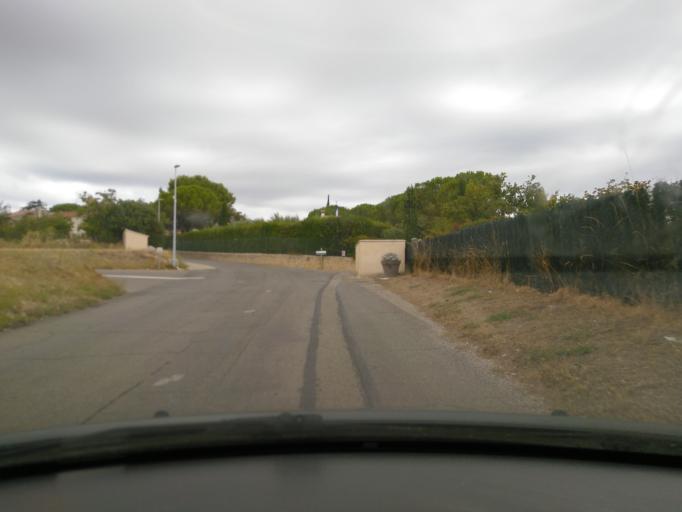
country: FR
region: Rhone-Alpes
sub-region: Departement de la Drome
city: Vinsobres
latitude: 44.3322
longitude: 5.0645
